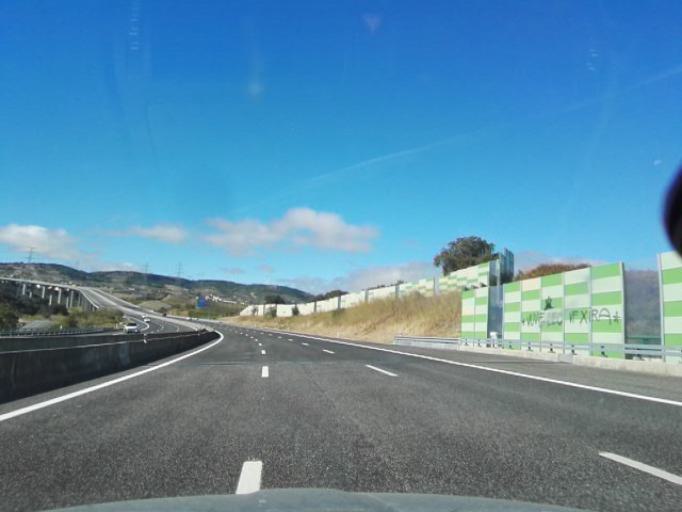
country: PT
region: Lisbon
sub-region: Arruda Dos Vinhos
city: Arruda dos Vinhos
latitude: 38.9870
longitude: -9.0486
